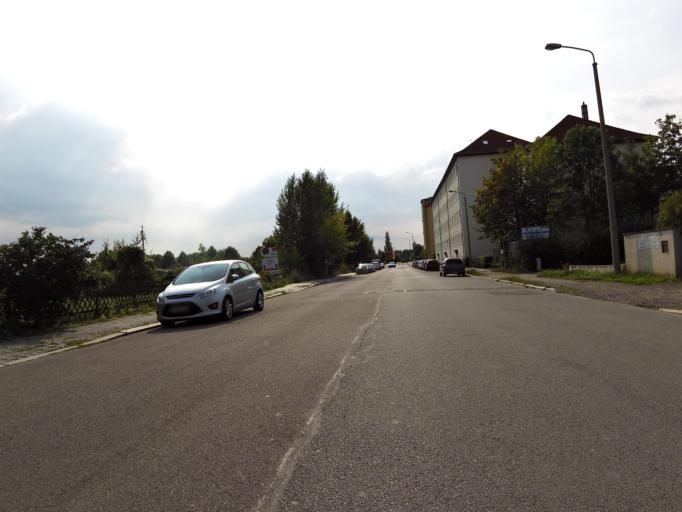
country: DE
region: Saxony
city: Leipzig
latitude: 51.3820
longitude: 12.3912
